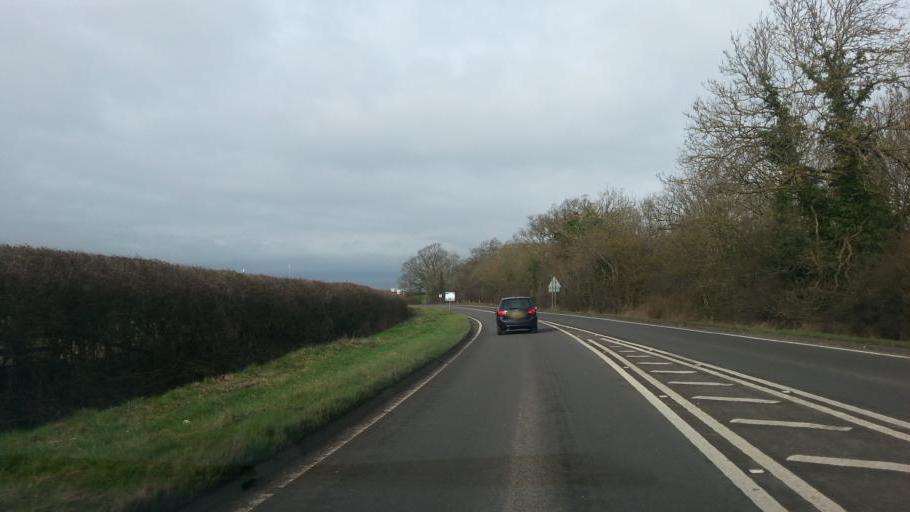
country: GB
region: England
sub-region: Nottinghamshire
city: Cotgrave
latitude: 52.8812
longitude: -1.0601
